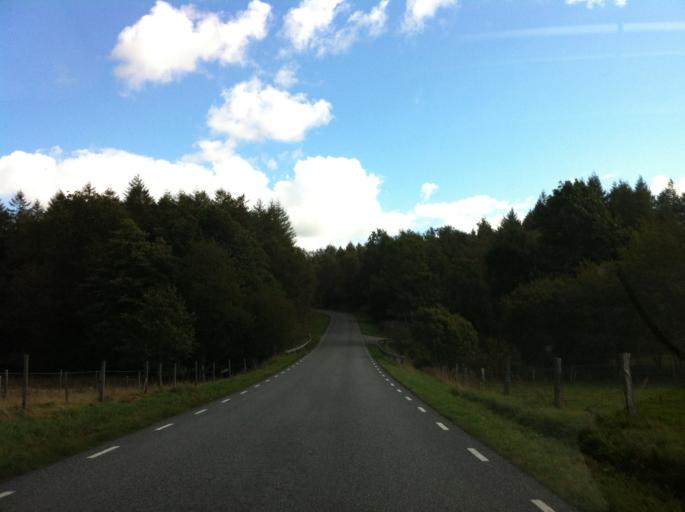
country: SE
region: Skane
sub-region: Kristianstads Kommun
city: Degeberga
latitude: 55.7082
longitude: 13.9862
